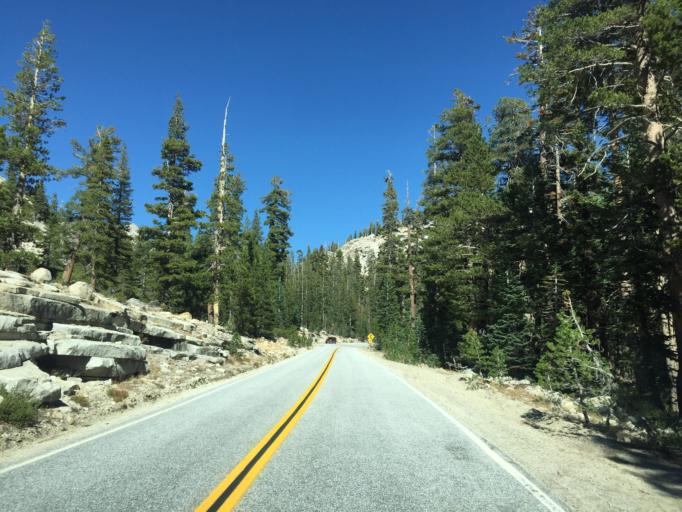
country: US
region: California
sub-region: Mariposa County
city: Yosemite Valley
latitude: 37.8166
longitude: -119.5183
